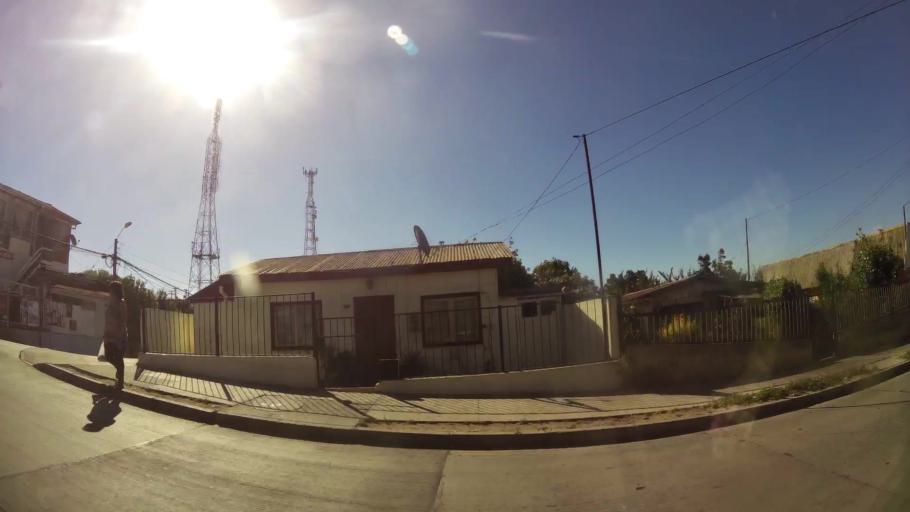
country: CL
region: Valparaiso
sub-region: Provincia de Valparaiso
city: Vina del Mar
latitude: -33.0484
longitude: -71.5604
